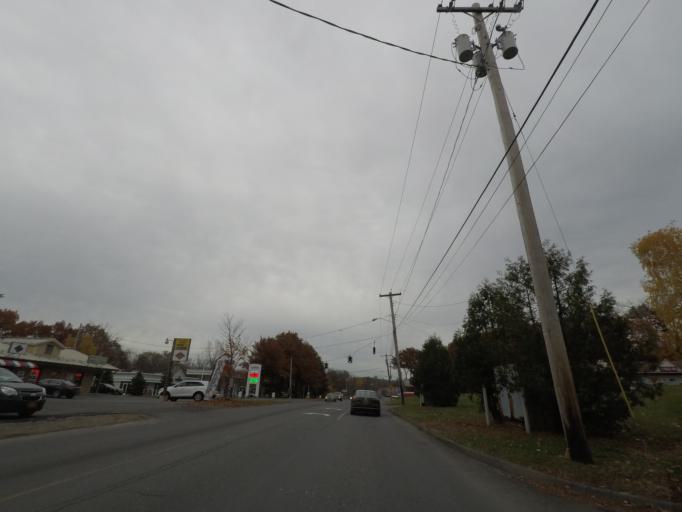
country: US
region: New York
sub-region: Rensselaer County
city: Troy
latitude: 42.7068
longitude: -73.6791
